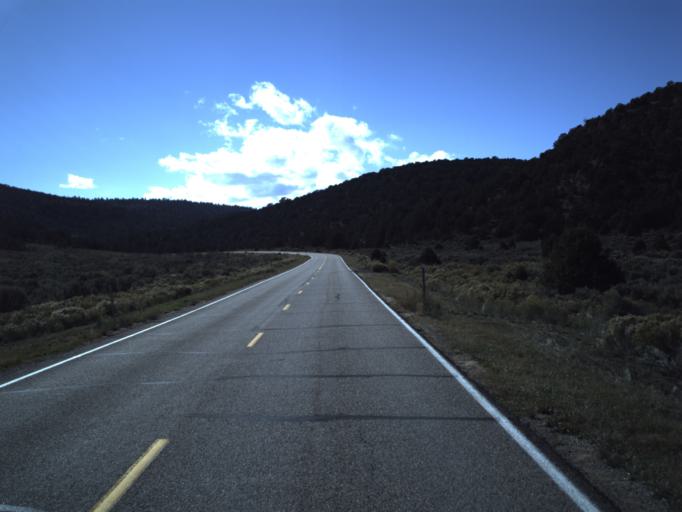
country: US
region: Utah
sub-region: Garfield County
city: Panguitch
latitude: 37.7649
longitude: -112.4962
